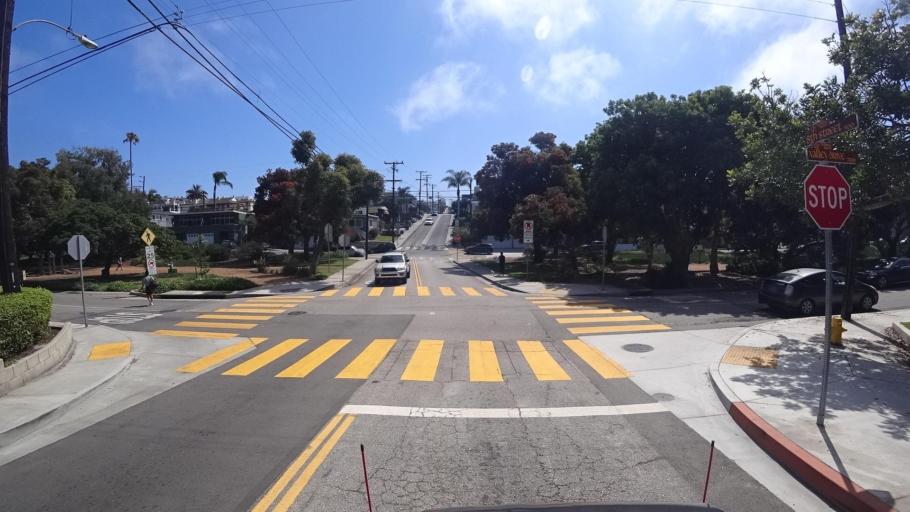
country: US
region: California
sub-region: Los Angeles County
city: Hermosa Beach
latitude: 33.8601
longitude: -118.3944
